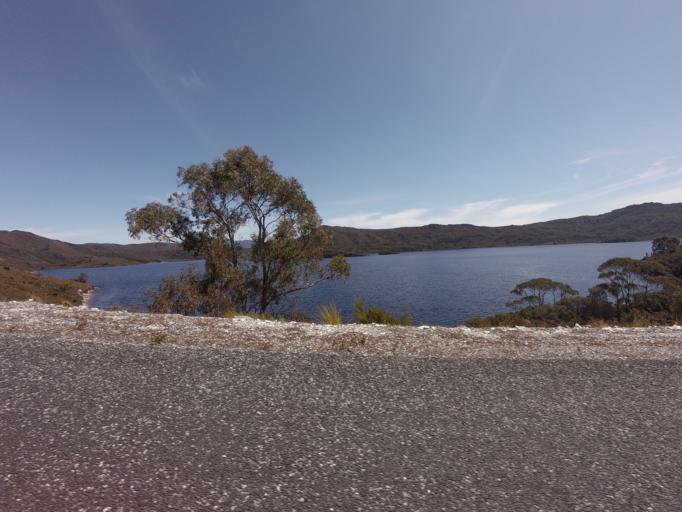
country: AU
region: Tasmania
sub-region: Huon Valley
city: Geeveston
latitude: -42.8352
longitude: 146.1273
